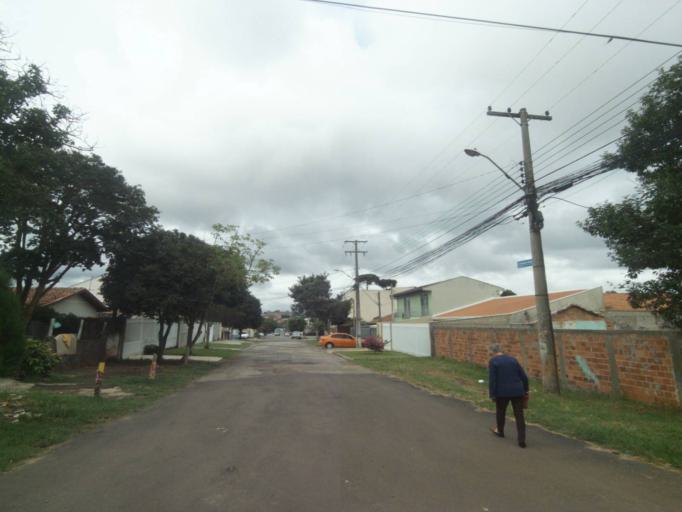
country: BR
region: Parana
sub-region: Curitiba
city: Curitiba
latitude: -25.4900
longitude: -49.3084
